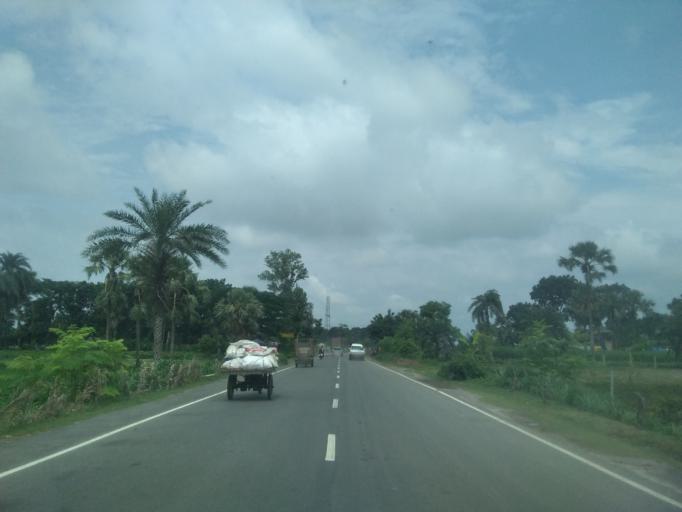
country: BD
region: Khulna
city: Kesabpur
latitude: 22.8165
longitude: 89.2549
